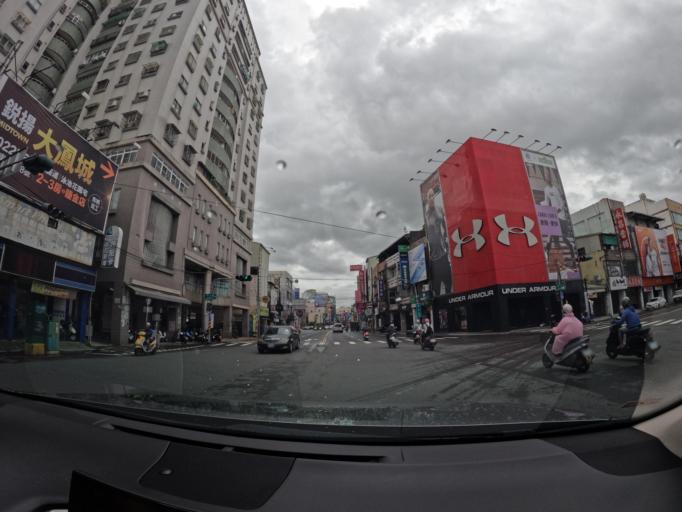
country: TW
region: Taiwan
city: Fengshan
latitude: 22.6259
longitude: 120.3565
